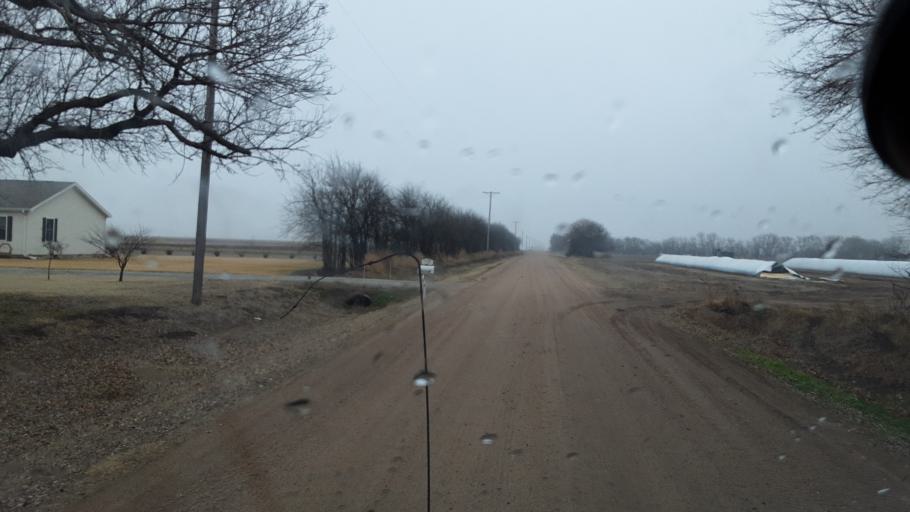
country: US
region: Kansas
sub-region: Reno County
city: South Hutchinson
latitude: 37.9555
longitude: -98.0185
